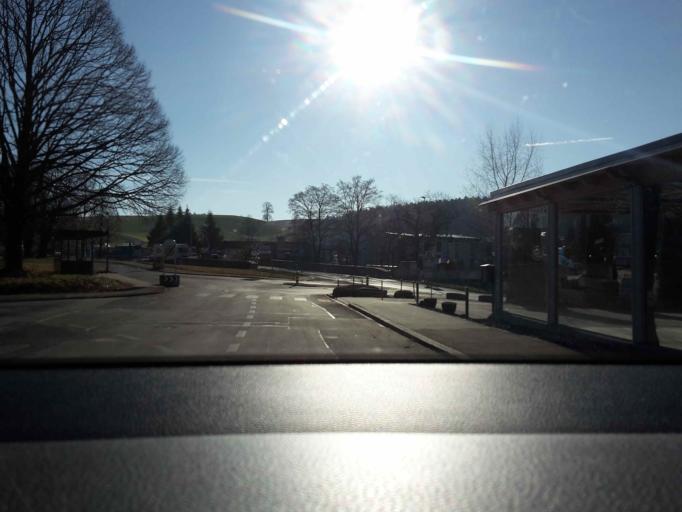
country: CH
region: Bern
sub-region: Oberaargau
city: Huttwil
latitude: 47.1149
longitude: 7.8621
